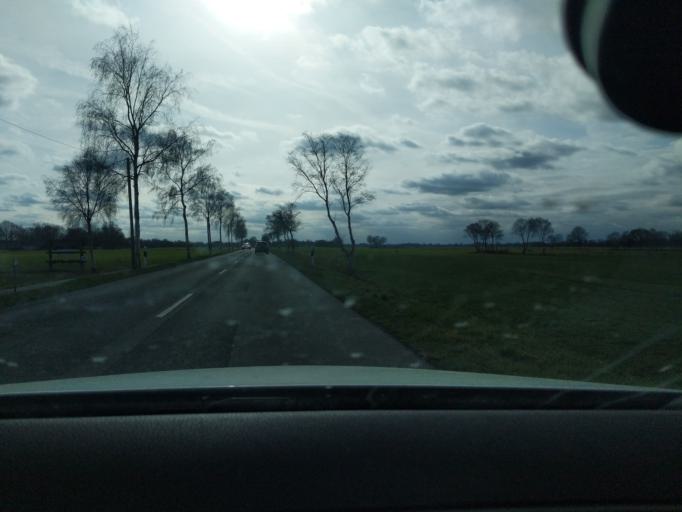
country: DE
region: Lower Saxony
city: Drochtersen
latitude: 53.6663
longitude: 9.3817
